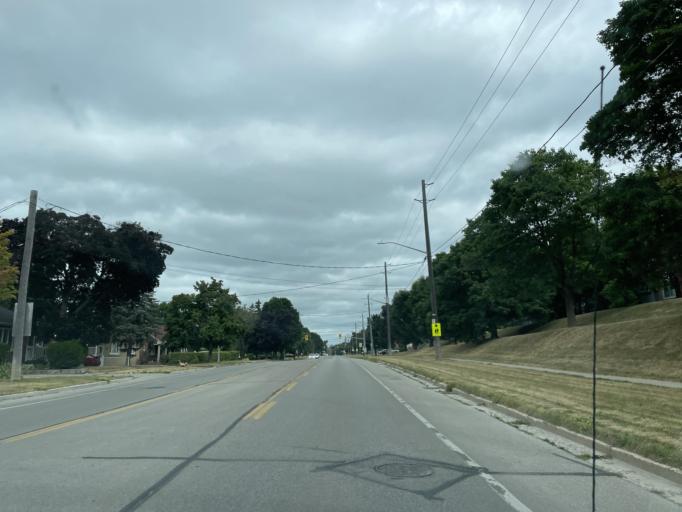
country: CA
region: Ontario
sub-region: Wellington County
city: Guelph
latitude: 43.5628
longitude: -80.2532
